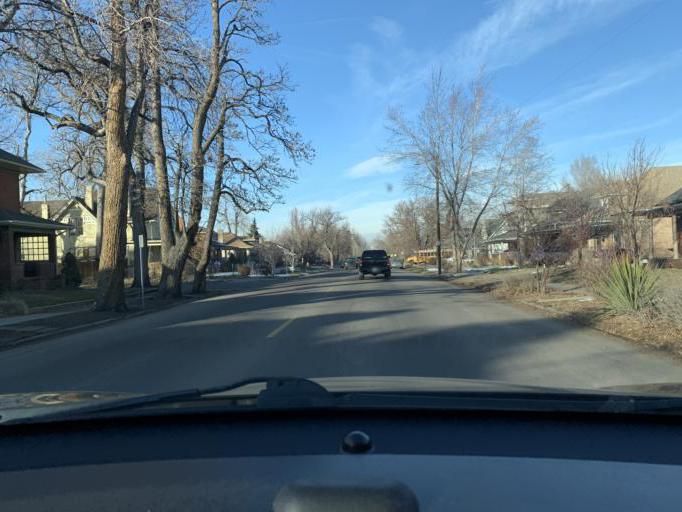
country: US
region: Colorado
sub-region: Adams County
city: Berkley
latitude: 39.7710
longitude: -105.0346
